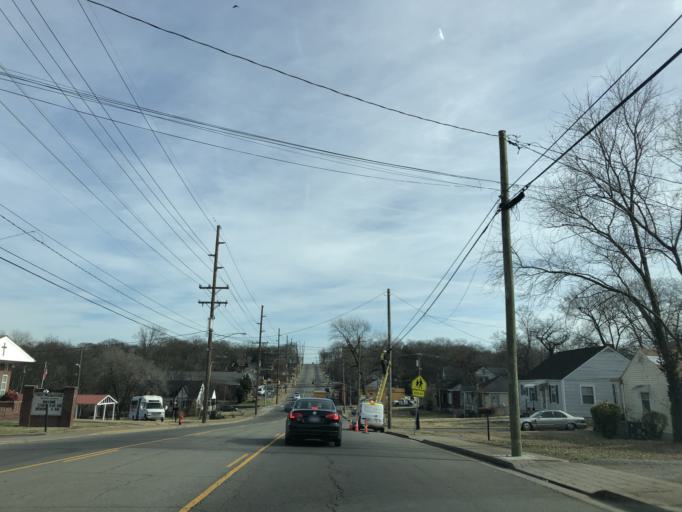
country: US
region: Tennessee
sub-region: Davidson County
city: Nashville
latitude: 36.2052
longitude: -86.7593
